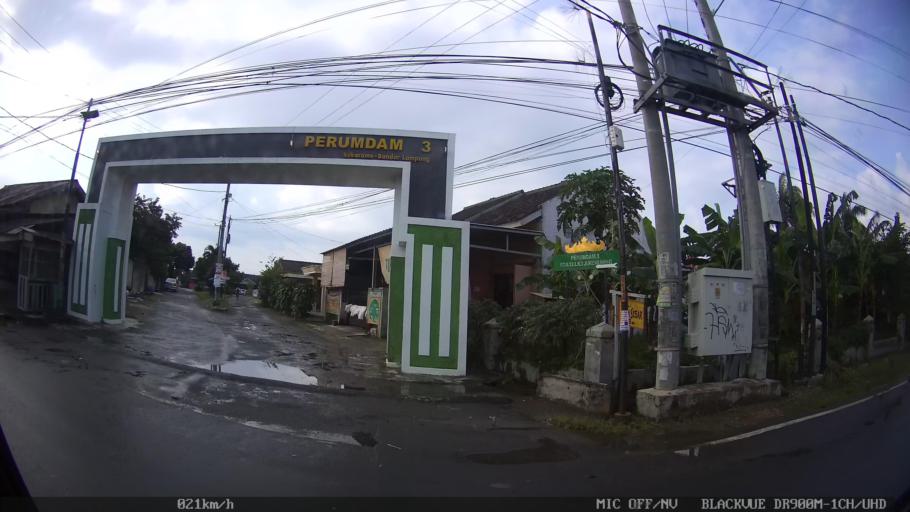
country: ID
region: Lampung
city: Kedaton
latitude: -5.3911
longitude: 105.3051
